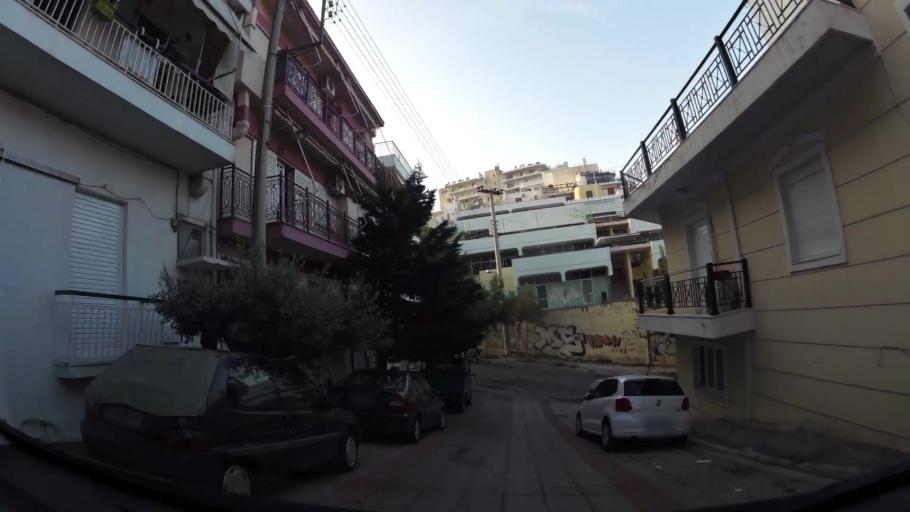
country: GR
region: Attica
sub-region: Nomarchia Athinas
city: Ymittos
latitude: 37.9512
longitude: 23.7547
